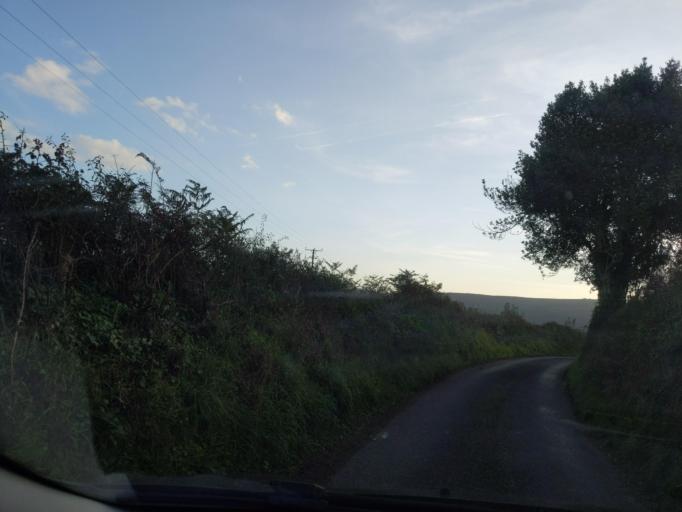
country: GB
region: England
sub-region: Devon
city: Bovey Tracey
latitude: 50.6218
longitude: -3.6930
